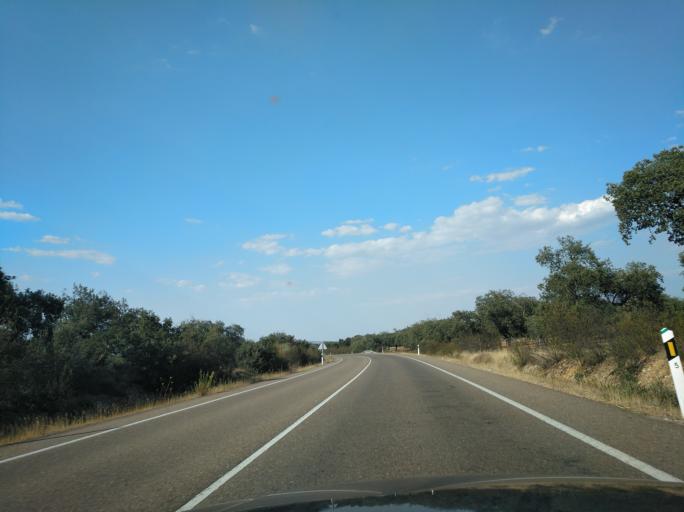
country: ES
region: Extremadura
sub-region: Provincia de Badajoz
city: Villanueva del Fresno
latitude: 38.4124
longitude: -7.1376
